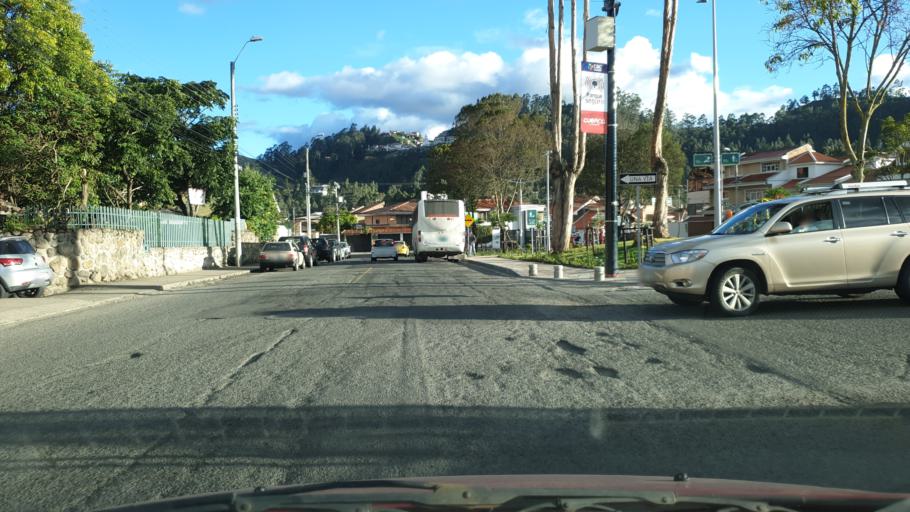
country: EC
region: Azuay
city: Cuenca
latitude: -2.9132
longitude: -79.0147
